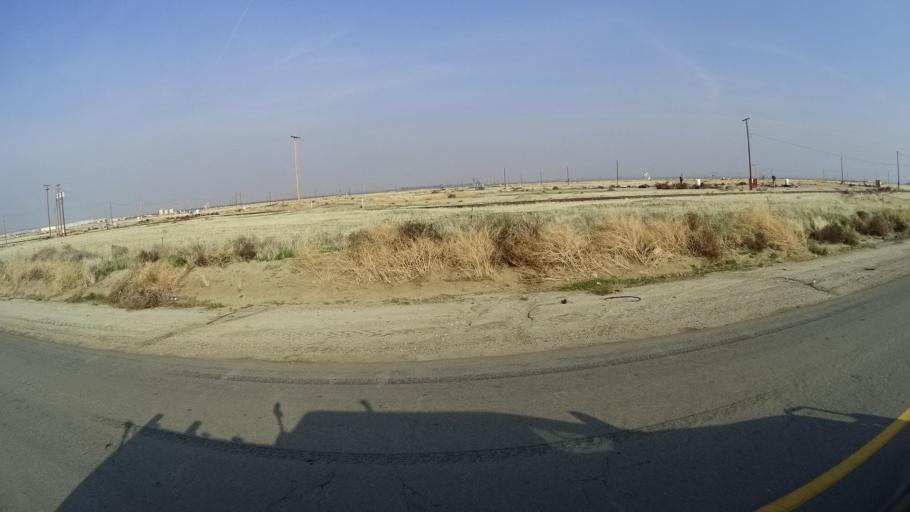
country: US
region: California
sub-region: Kern County
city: Lebec
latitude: 34.9845
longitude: -118.9221
